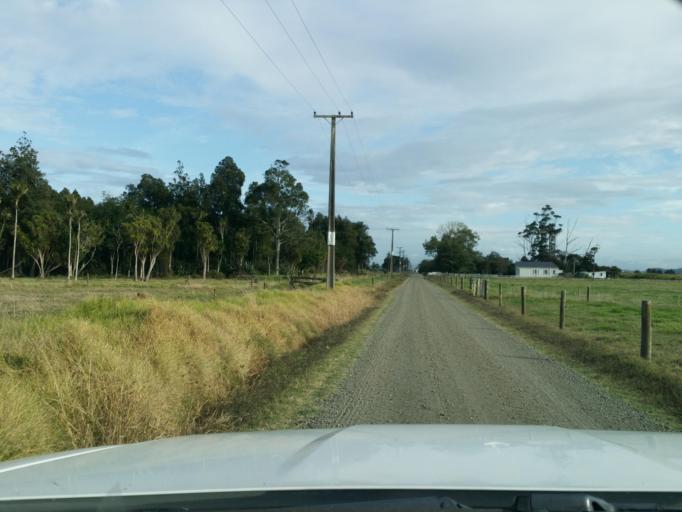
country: NZ
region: Northland
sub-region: Kaipara District
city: Dargaville
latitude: -36.0634
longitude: 173.9482
